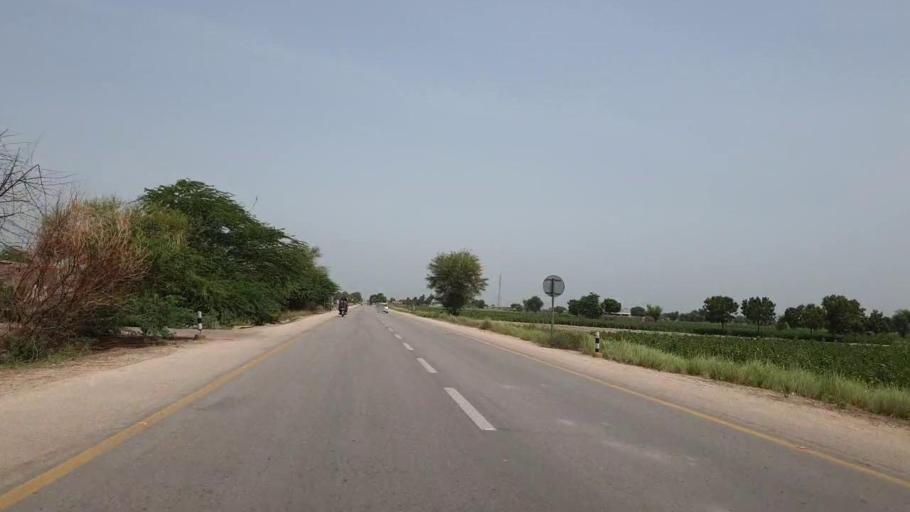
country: PK
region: Sindh
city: Shahpur Chakar
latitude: 26.1510
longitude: 68.6358
